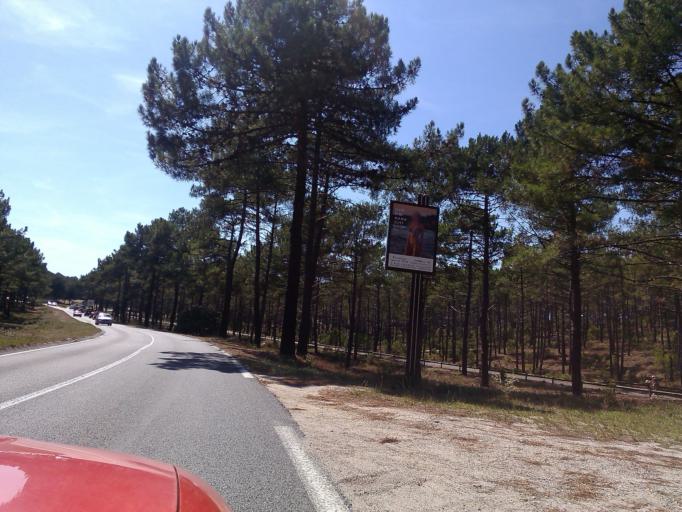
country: FR
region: Aquitaine
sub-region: Departement de la Gironde
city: Lacanau
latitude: 45.0059
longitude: -1.1785
